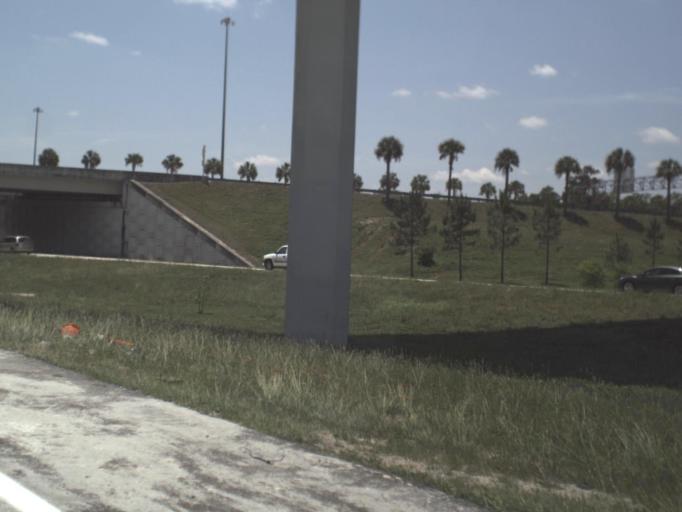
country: US
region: Florida
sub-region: Saint Johns County
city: Fruit Cove
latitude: 30.1677
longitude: -81.5560
